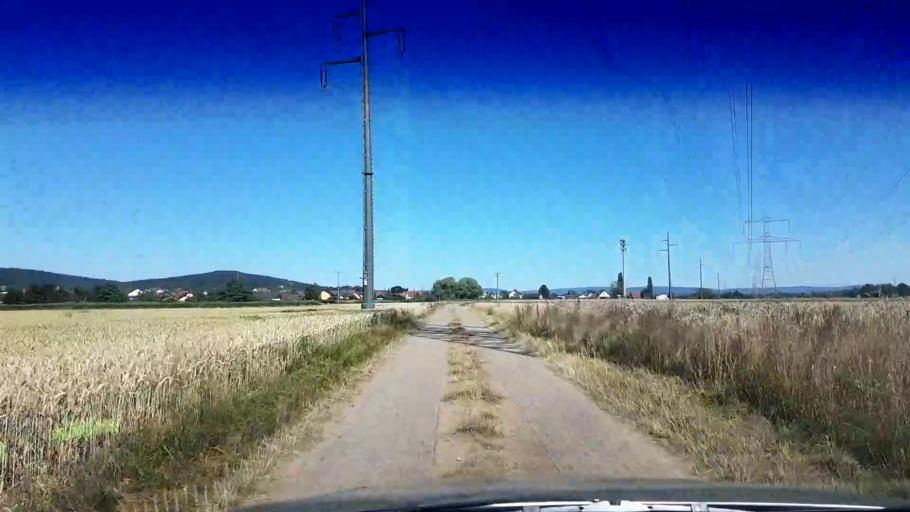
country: DE
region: Bavaria
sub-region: Upper Franconia
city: Oberhaid
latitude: 49.9293
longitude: 10.8038
